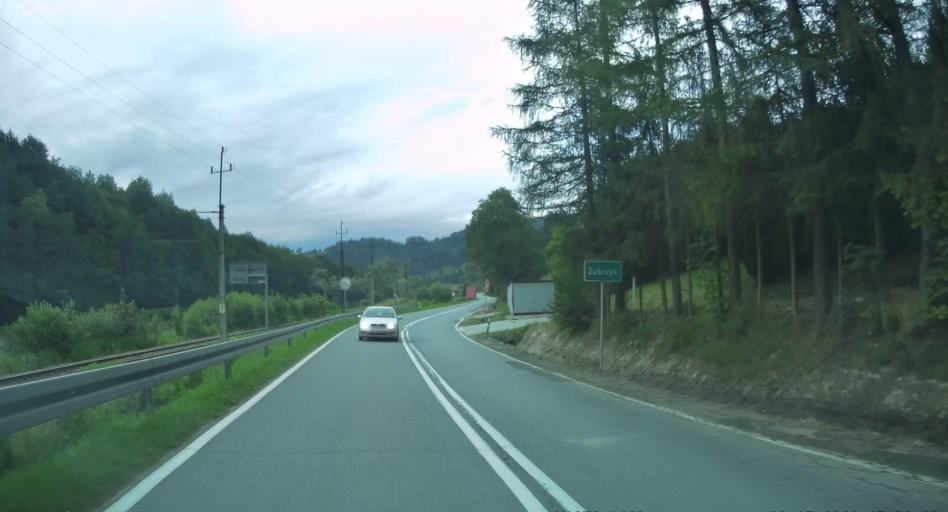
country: PL
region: Lesser Poland Voivodeship
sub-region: Powiat nowosadecki
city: Piwniczna-Zdroj
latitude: 49.3760
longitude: 20.7588
